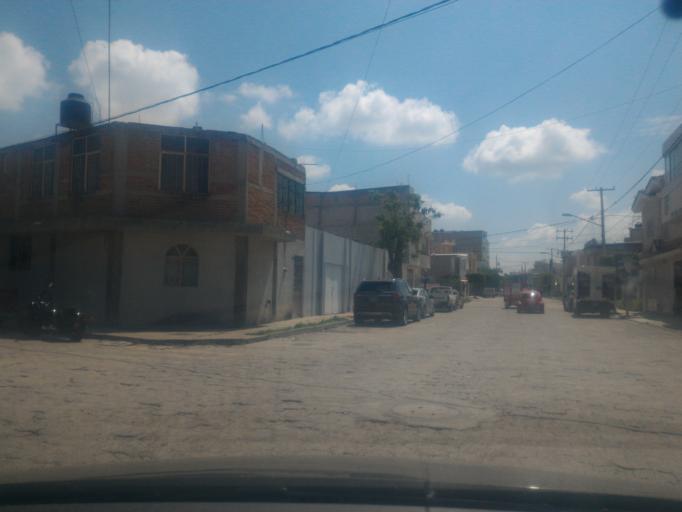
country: MX
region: Guanajuato
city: San Francisco del Rincon
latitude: 21.0092
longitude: -101.8584
